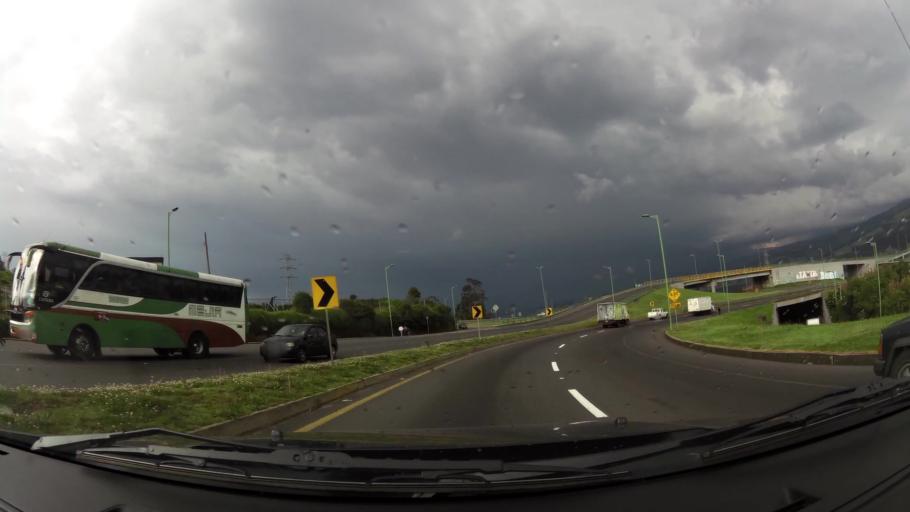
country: EC
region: Pichincha
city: Sangolqui
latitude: -0.3841
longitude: -78.5334
